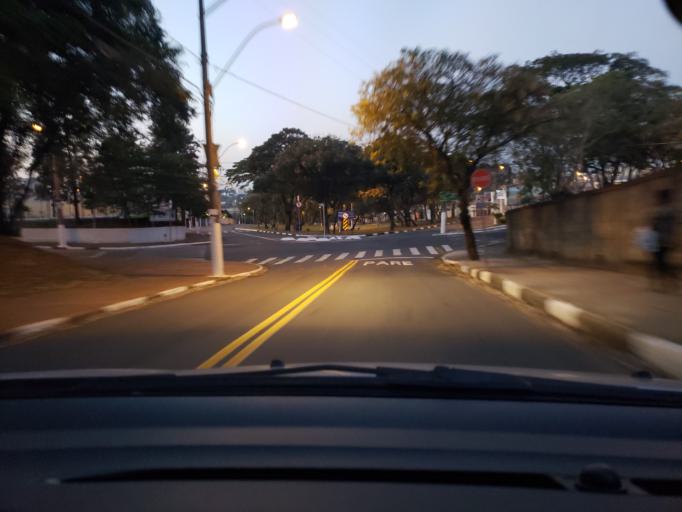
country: BR
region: Sao Paulo
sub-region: Campinas
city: Campinas
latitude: -22.9145
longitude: -47.1094
